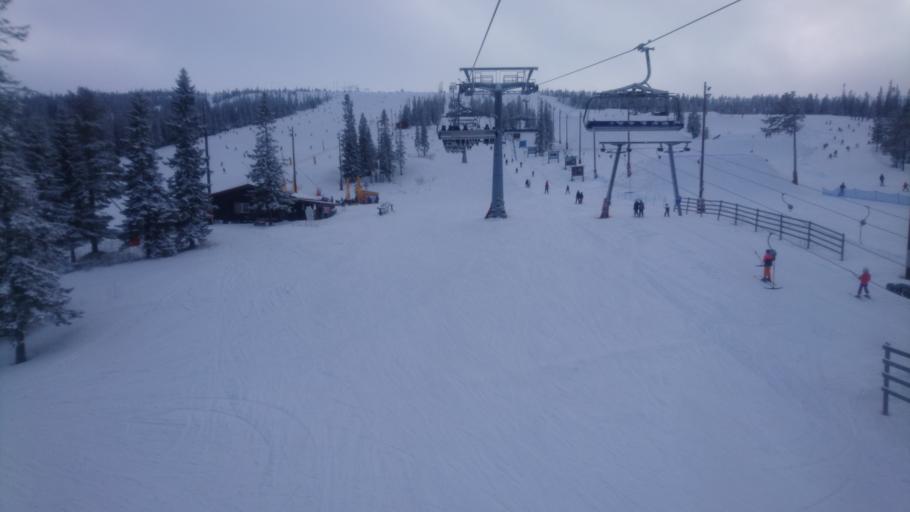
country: SE
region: Dalarna
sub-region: Malung-Saelens kommun
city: Malung
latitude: 61.1610
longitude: 13.1875
